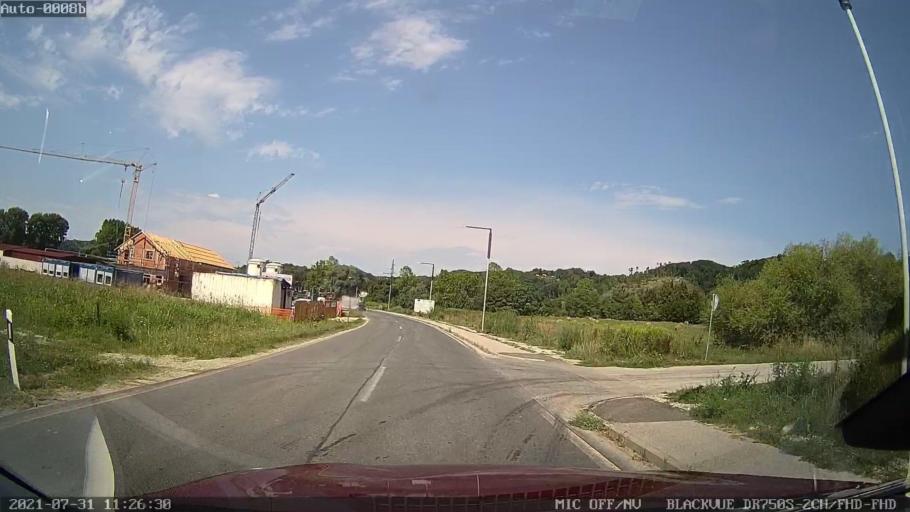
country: HR
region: Varazdinska
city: Jalzabet
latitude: 46.2106
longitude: 16.4405
